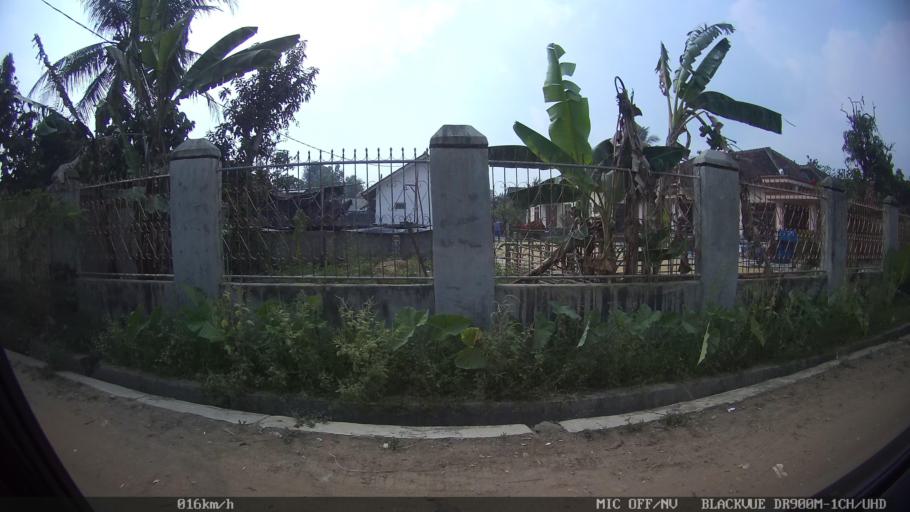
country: ID
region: Lampung
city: Pringsewu
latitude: -5.3677
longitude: 104.9985
